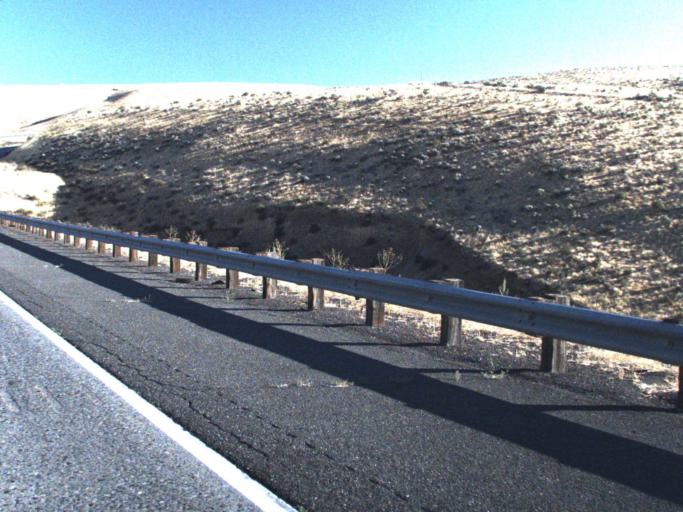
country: US
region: Washington
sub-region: Yakima County
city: Terrace Heights
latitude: 46.7447
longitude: -120.3882
